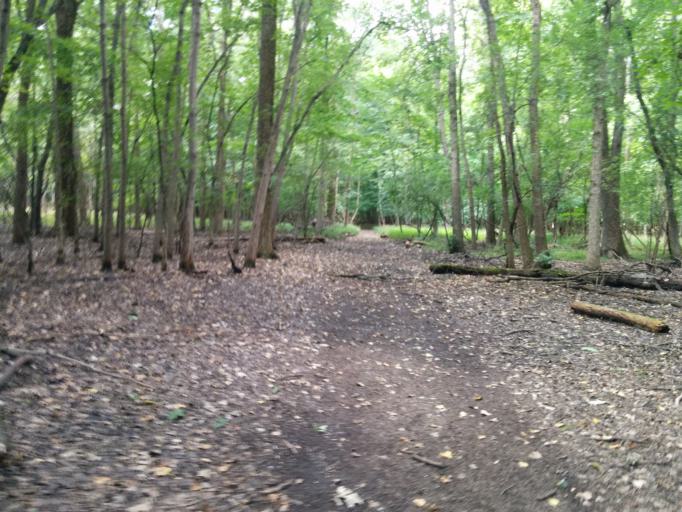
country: US
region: Illinois
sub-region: Lake County
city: Riverwoods
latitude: 42.1503
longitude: -87.9027
